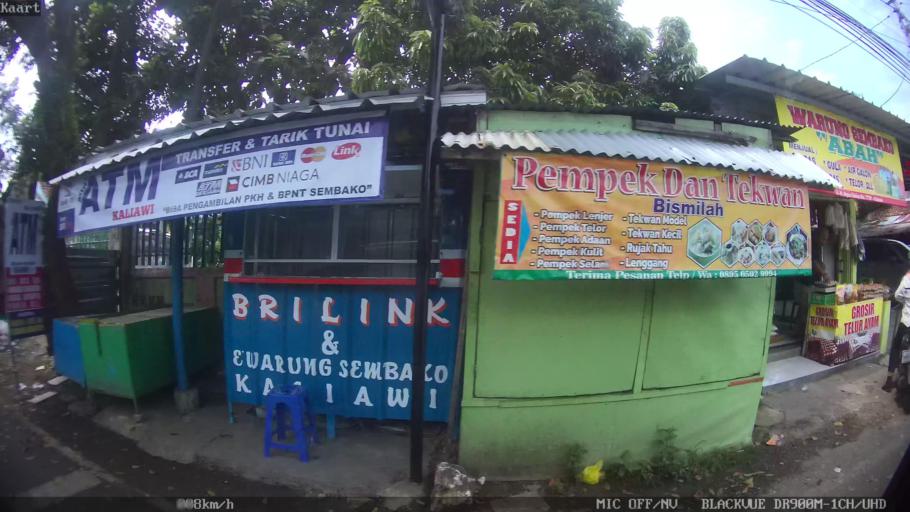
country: ID
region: Lampung
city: Bandarlampung
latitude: -5.4123
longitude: 105.2522
